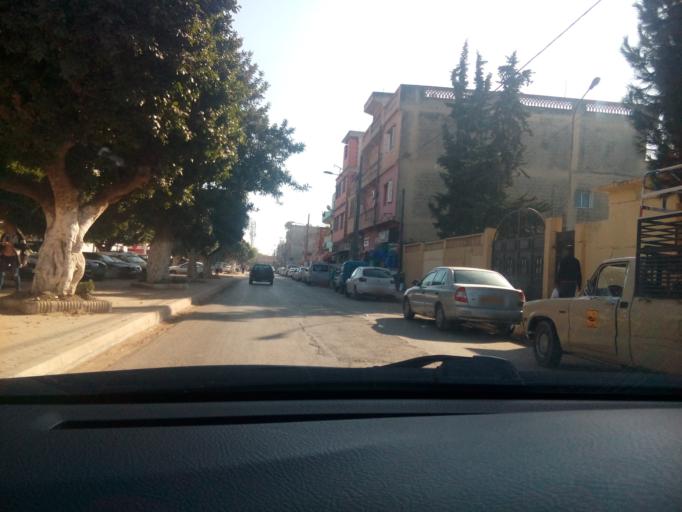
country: DZ
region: Oran
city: Es Senia
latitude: 35.6499
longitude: -0.6262
